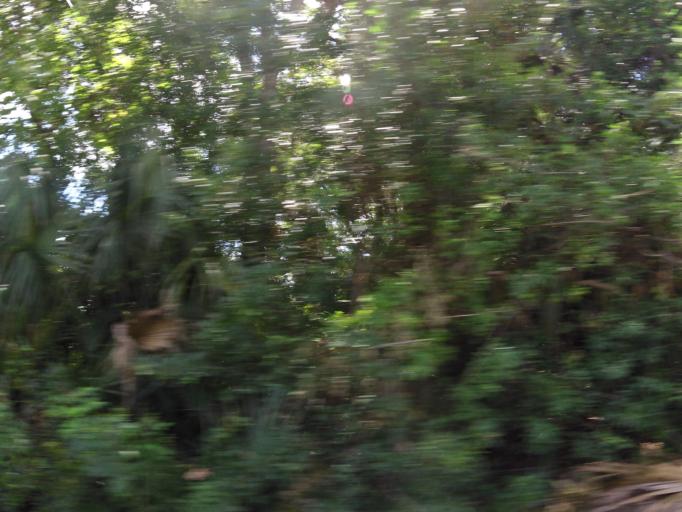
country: US
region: Florida
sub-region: Brevard County
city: Mims
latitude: 28.6371
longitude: -80.8455
